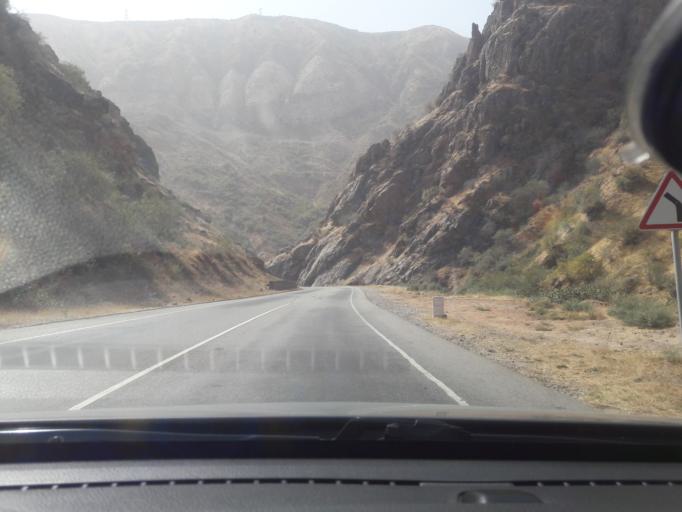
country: TJ
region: Khatlon
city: Norak
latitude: 38.4308
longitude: 69.2084
